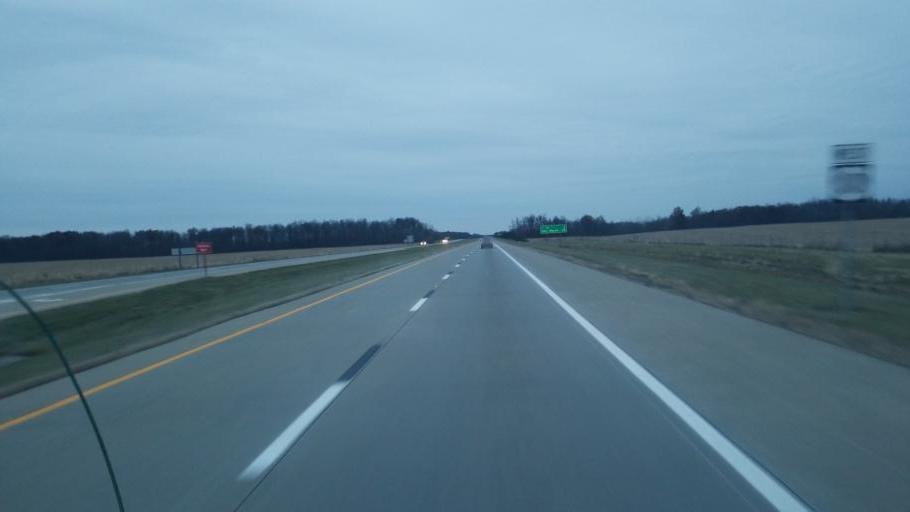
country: US
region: Ohio
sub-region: Hardin County
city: Ada
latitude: 40.8276
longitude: -83.8434
